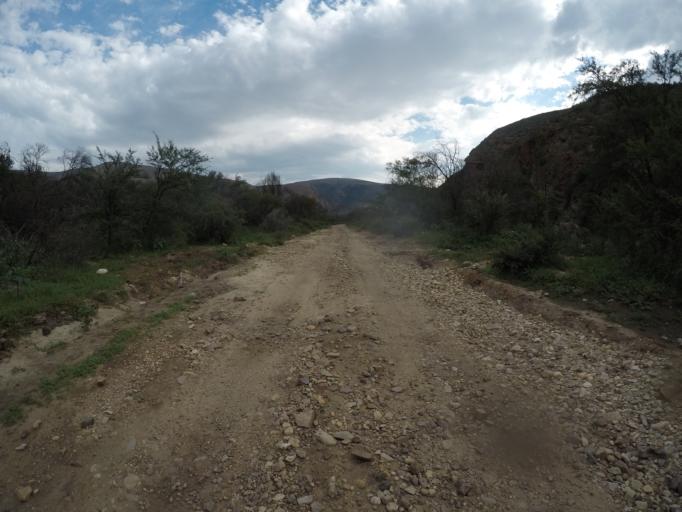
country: ZA
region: Eastern Cape
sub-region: Cacadu District Municipality
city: Kareedouw
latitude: -33.6028
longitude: 24.2062
